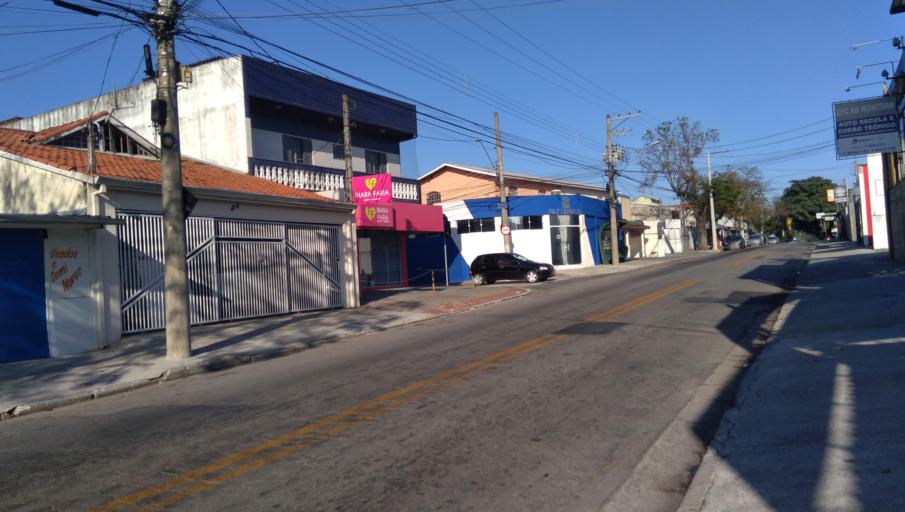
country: BR
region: Sao Paulo
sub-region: Sao Jose Dos Campos
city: Sao Jose dos Campos
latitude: -23.1744
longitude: -45.8228
